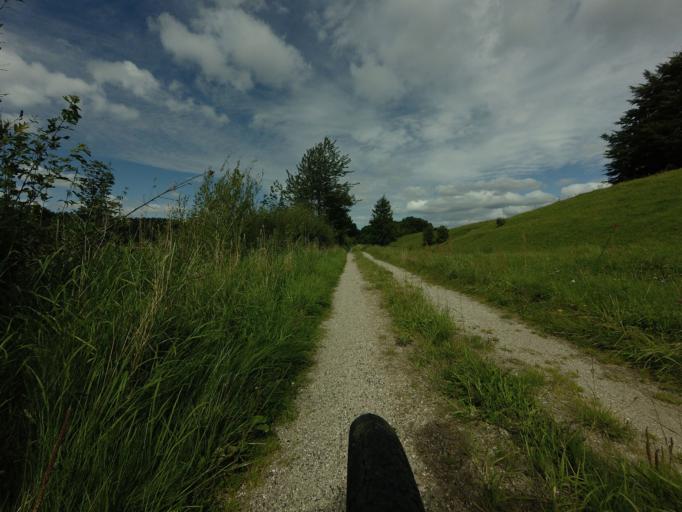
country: DK
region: Central Jutland
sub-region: Syddjurs Kommune
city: Ryomgard
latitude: 56.3934
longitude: 10.5316
